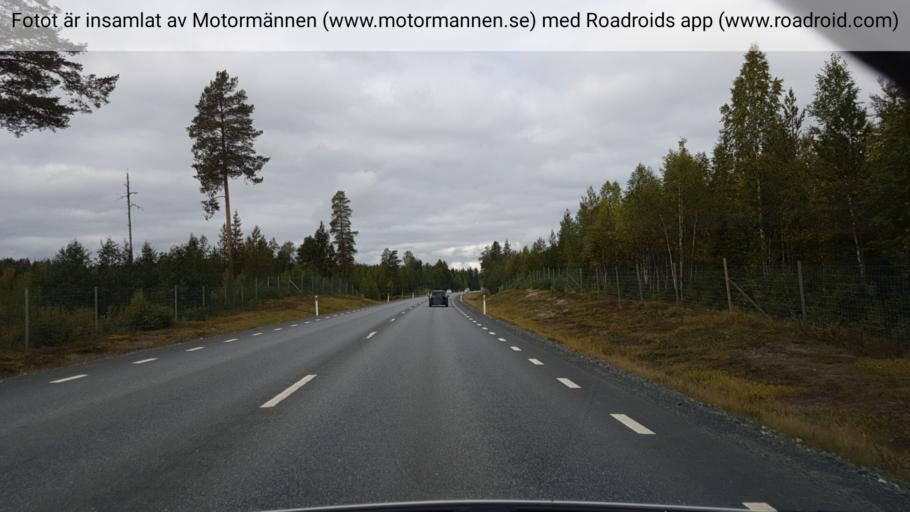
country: SE
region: Vaesterbotten
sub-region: Skelleftea Kommun
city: Forsbacka
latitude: 64.8292
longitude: 20.5566
